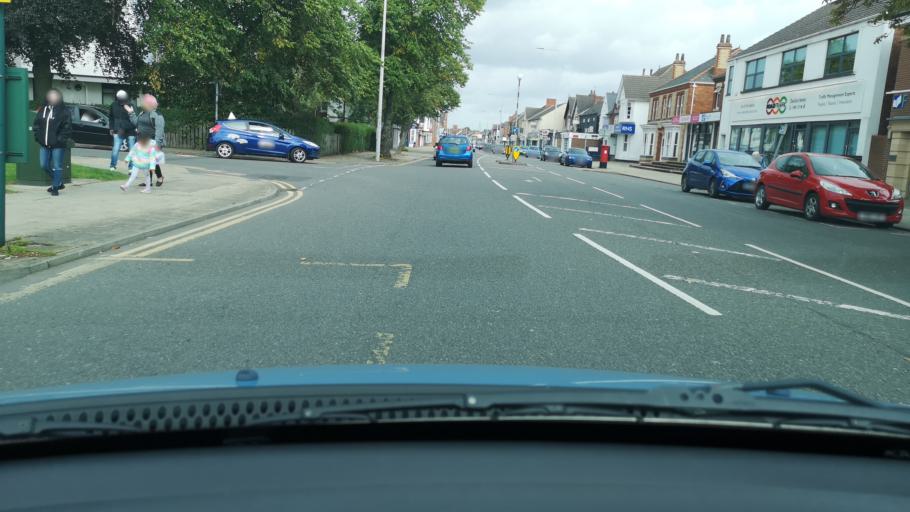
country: GB
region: England
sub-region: North Lincolnshire
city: Scunthorpe
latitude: 53.5883
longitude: -0.6538
